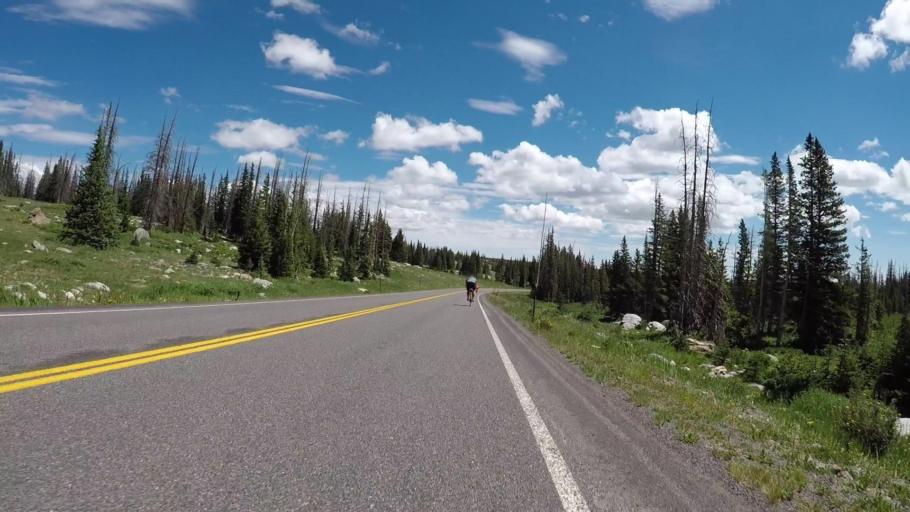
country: US
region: Wyoming
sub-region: Carbon County
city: Saratoga
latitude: 41.3524
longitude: -106.2500
